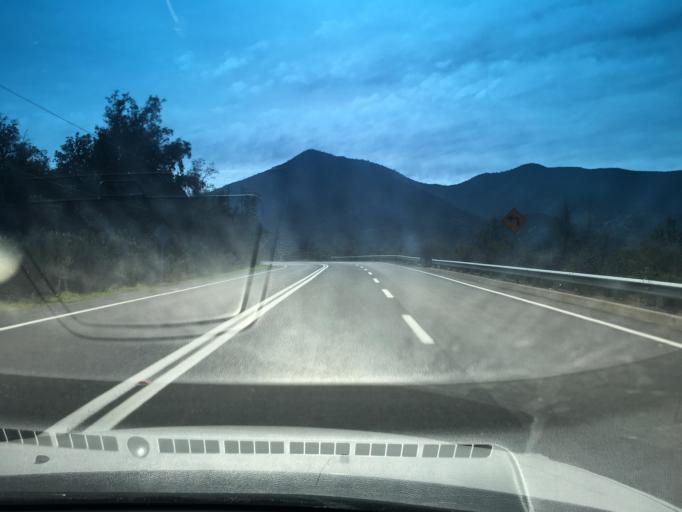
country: CL
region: Valparaiso
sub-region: Provincia de San Felipe
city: Llaillay
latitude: -33.0639
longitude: -70.9876
